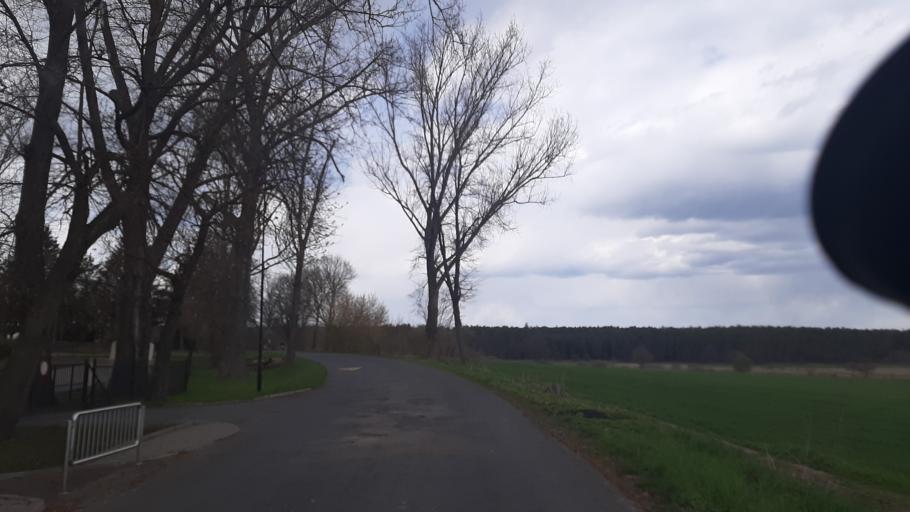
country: PL
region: Lublin Voivodeship
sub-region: Powiat lubelski
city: Niemce
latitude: 51.3635
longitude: 22.5542
